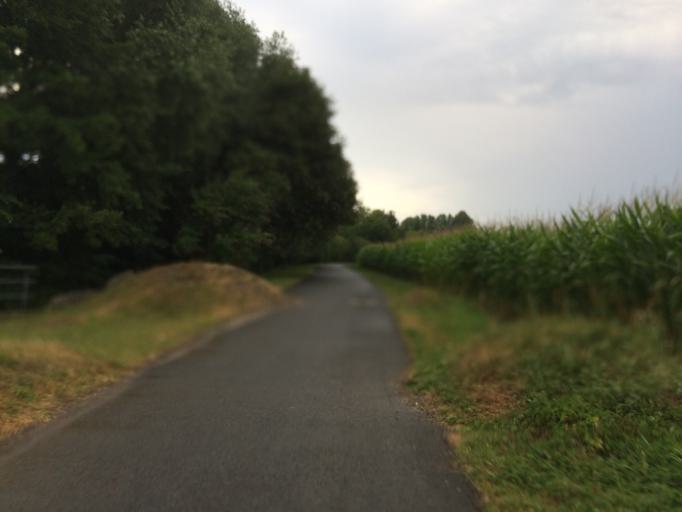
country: FR
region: Picardie
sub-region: Departement de l'Oise
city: Jaux
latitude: 49.3790
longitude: 2.7780
